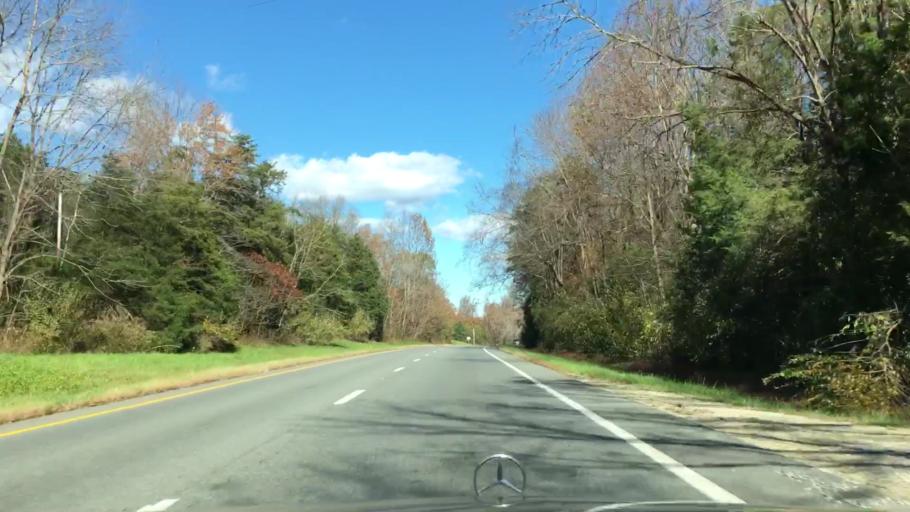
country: US
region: Virginia
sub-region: Albemarle County
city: Crozet
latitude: 37.9201
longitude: -78.6823
